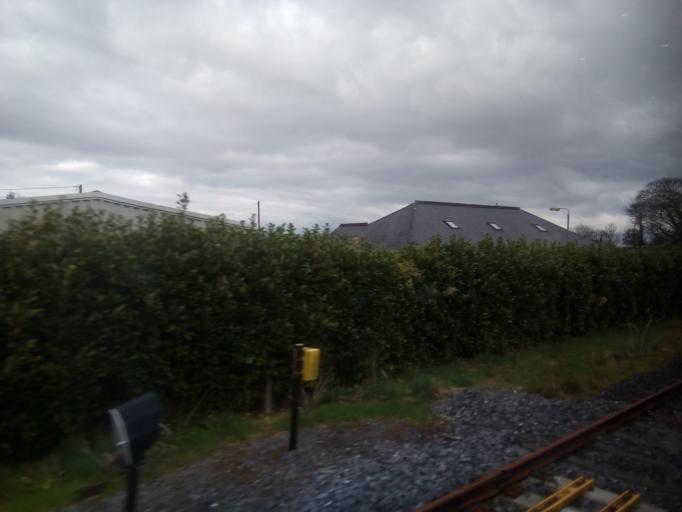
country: IE
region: Leinster
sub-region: An Longfort
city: Edgeworthstown
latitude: 53.6886
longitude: -7.5980
